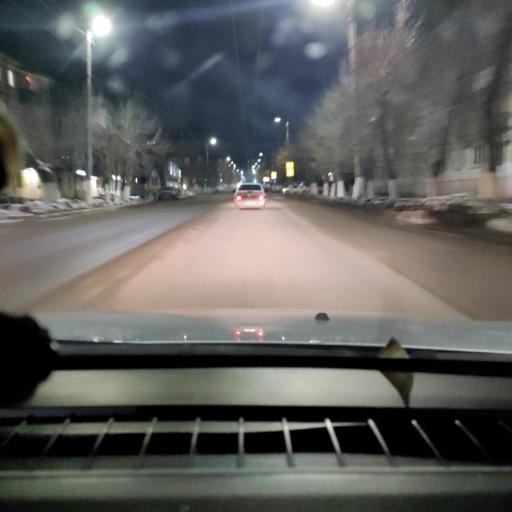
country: RU
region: Samara
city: Novokuybyshevsk
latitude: 53.0900
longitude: 49.9501
